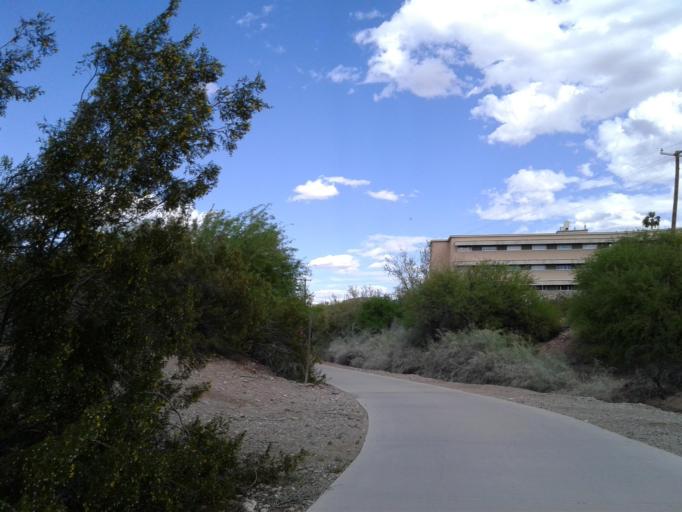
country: US
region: Arizona
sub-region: Maricopa County
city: Tempe Junction
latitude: 33.4404
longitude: -111.9424
